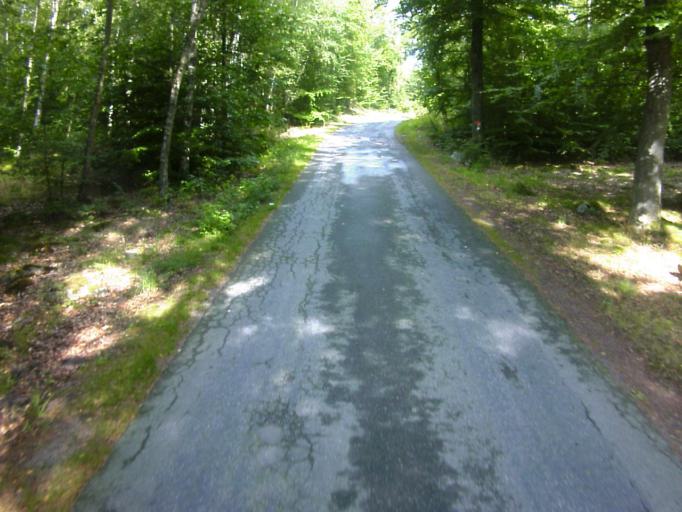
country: SE
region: Blekinge
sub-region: Solvesborgs Kommun
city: Soelvesborg
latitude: 56.0591
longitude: 14.5748
